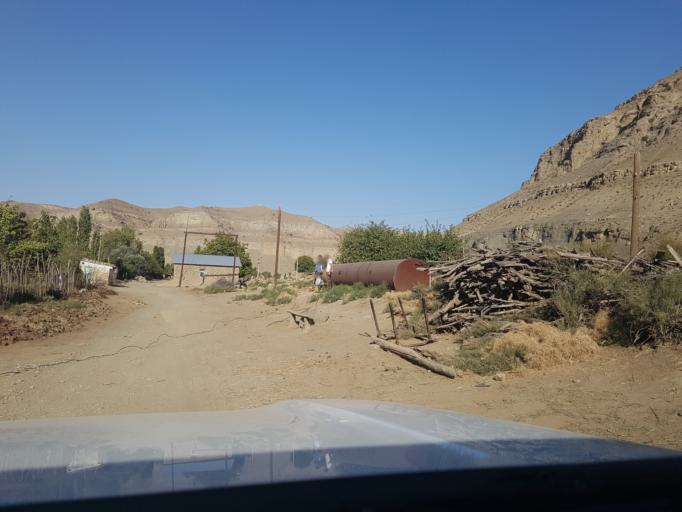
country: TM
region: Balkan
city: Magtymguly
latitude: 38.3005
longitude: 56.7507
